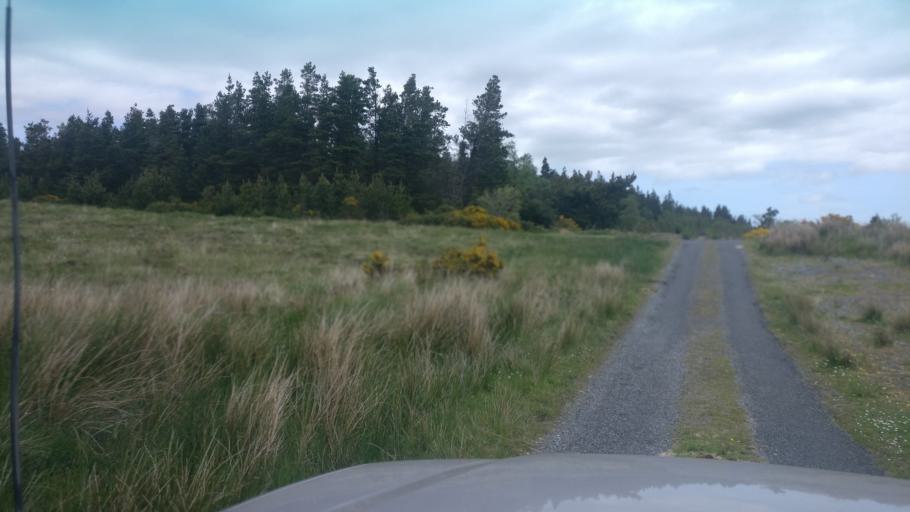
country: IE
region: Connaught
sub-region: County Galway
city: Loughrea
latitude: 53.1129
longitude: -8.6191
